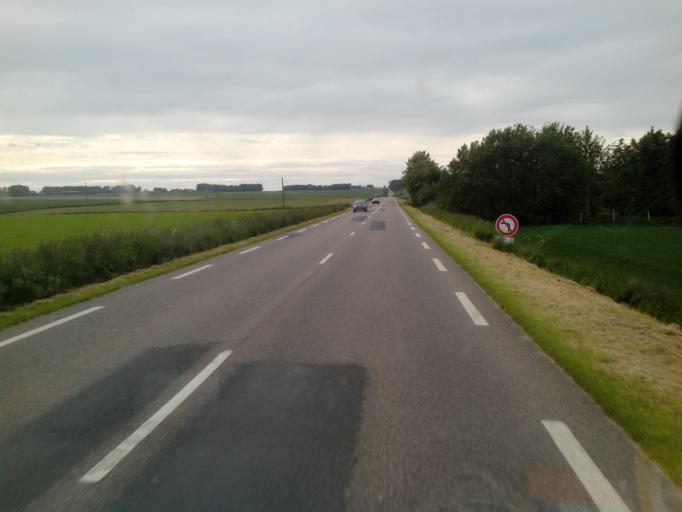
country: FR
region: Haute-Normandie
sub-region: Departement de la Seine-Maritime
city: Fauville-en-Caux
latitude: 49.6739
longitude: 0.5695
